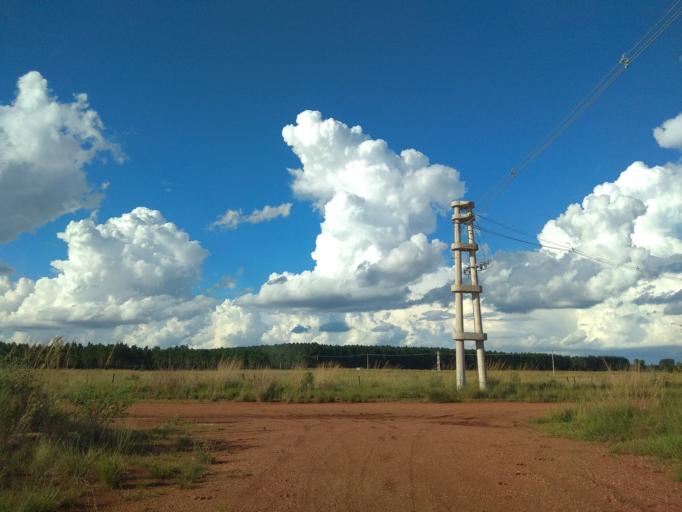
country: AR
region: Misiones
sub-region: Departamento de Candelaria
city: Candelaria
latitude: -27.4959
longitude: -55.7716
